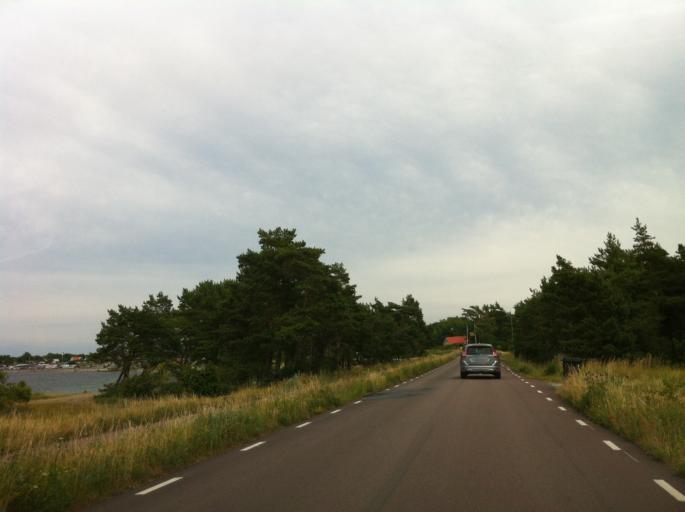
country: SE
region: Kalmar
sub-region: Oskarshamns Kommun
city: Oskarshamn
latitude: 57.3221
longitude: 17.0022
